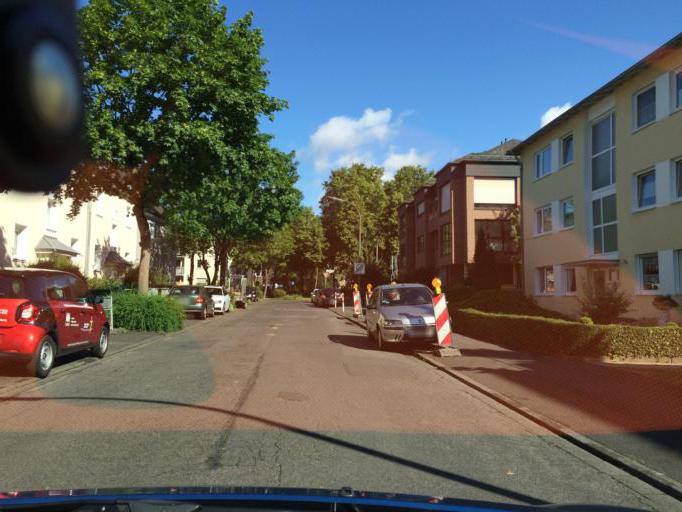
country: DE
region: North Rhine-Westphalia
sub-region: Regierungsbezirk Koln
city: Konigswinter
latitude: 50.6947
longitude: 7.1578
